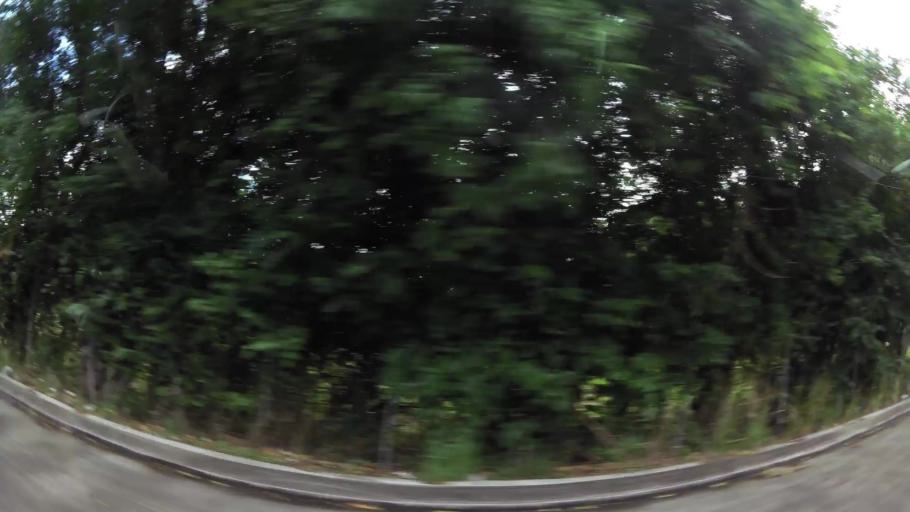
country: MQ
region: Martinique
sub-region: Martinique
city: Ducos
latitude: 14.5214
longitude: -60.9833
